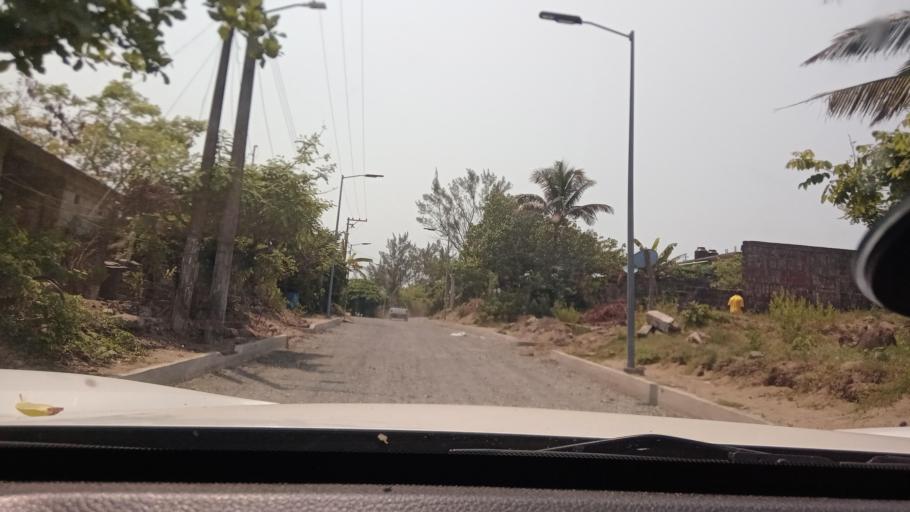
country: MX
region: Veracruz
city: Catemaco
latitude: 18.5567
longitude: -94.9917
